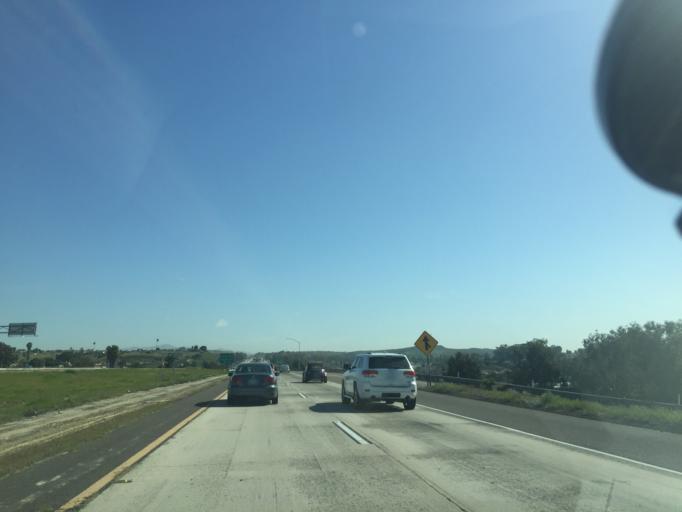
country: US
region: California
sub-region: San Diego County
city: Imperial Beach
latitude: 32.5682
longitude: -117.0609
